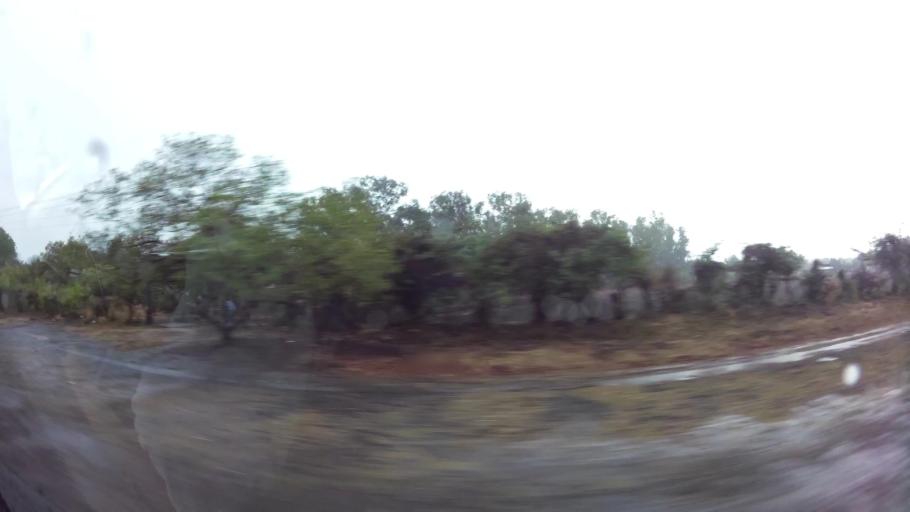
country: NI
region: Leon
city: Telica
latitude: 12.5304
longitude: -86.8539
